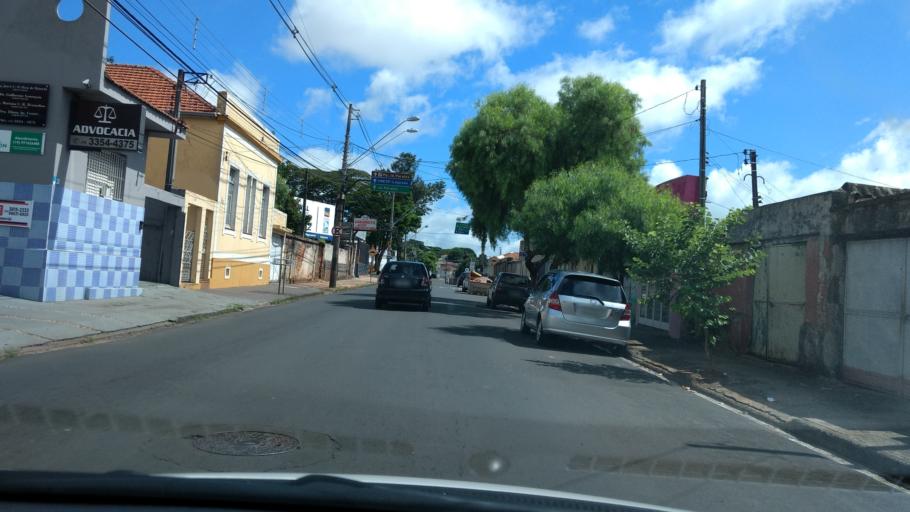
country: BR
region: Sao Paulo
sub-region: Botucatu
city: Botucatu
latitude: -22.8742
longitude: -48.4454
